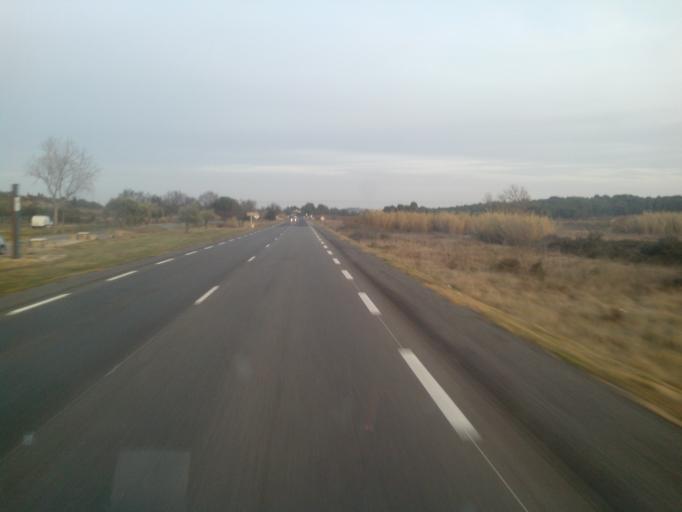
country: FR
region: Languedoc-Roussillon
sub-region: Departement de l'Herault
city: Olonzac
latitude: 43.2746
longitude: 2.7854
